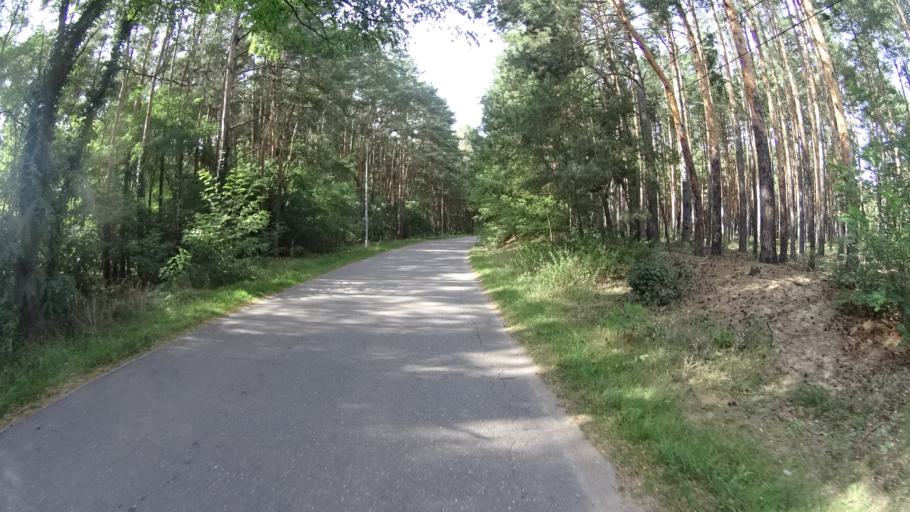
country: PL
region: Masovian Voivodeship
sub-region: Powiat legionowski
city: Serock
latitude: 52.4788
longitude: 21.0877
